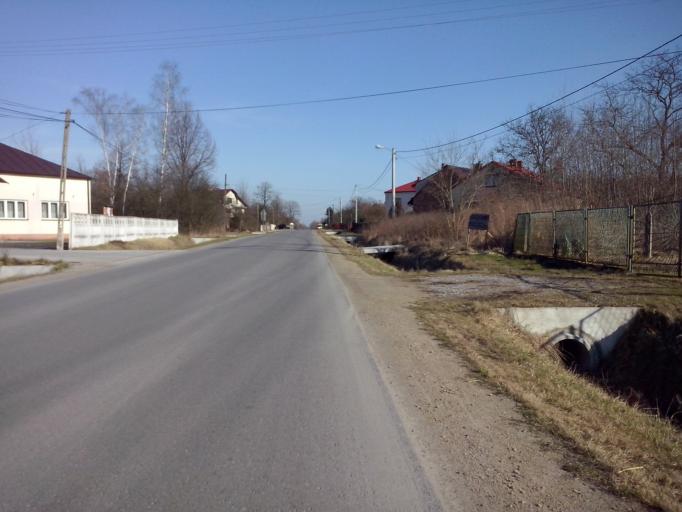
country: PL
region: Subcarpathian Voivodeship
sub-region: Powiat nizanski
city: Krzeszow
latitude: 50.4158
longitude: 22.3560
